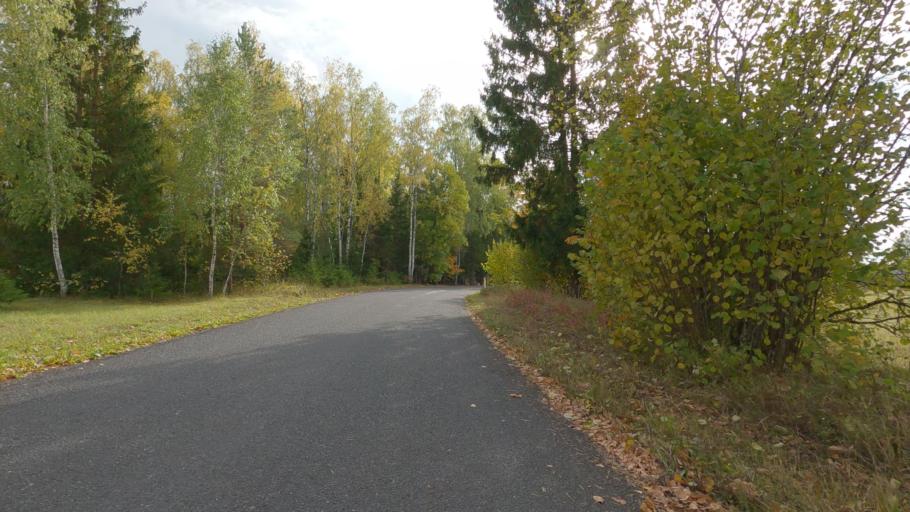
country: EE
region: Raplamaa
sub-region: Rapla vald
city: Rapla
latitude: 58.9791
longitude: 24.7849
